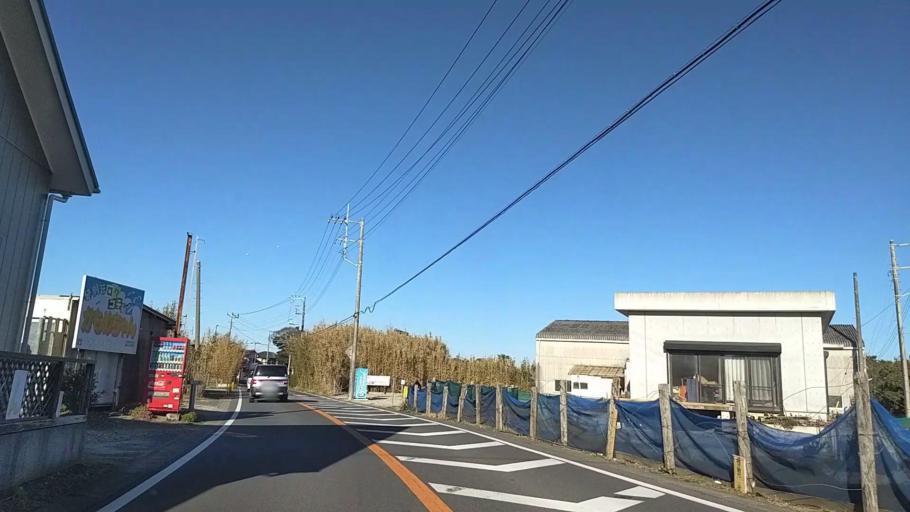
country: JP
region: Chiba
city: Naruto
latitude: 35.5585
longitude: 140.4710
